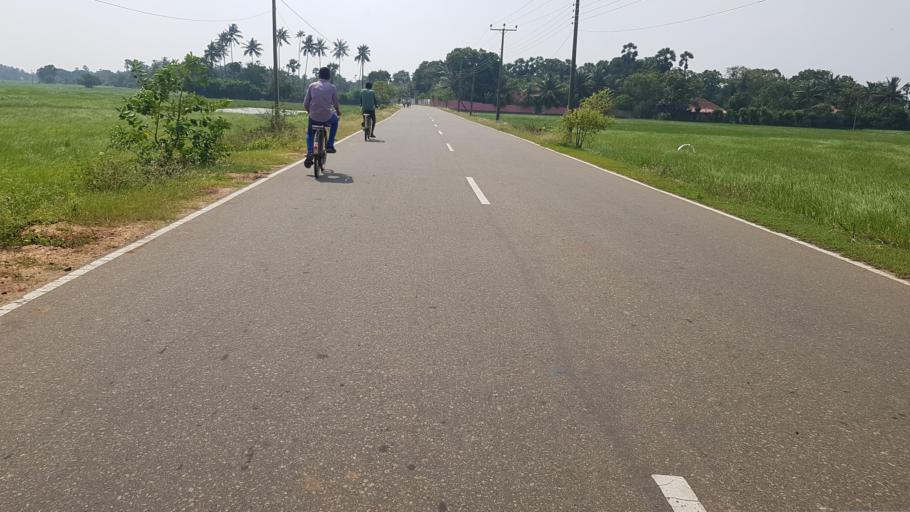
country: LK
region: Northern Province
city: Jaffna
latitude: 9.7265
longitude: 79.9479
